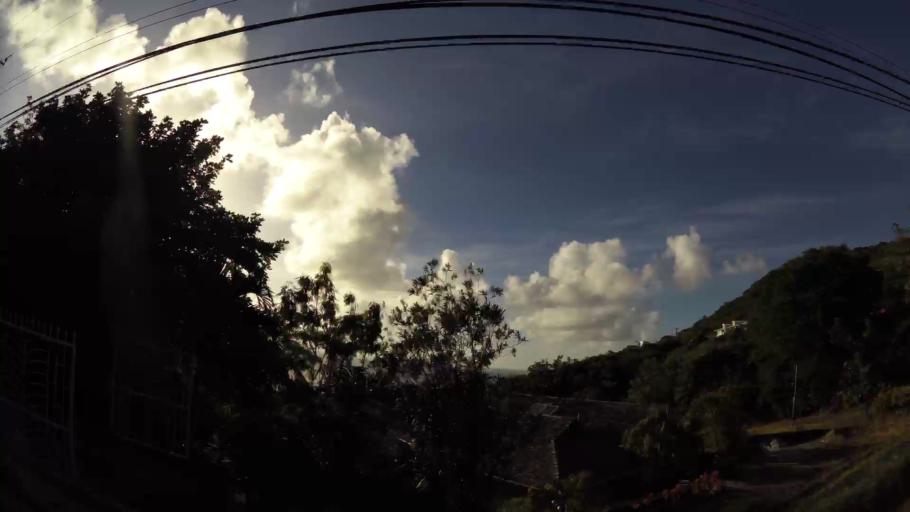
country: LC
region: Gros-Islet
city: Gros Islet
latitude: 14.1034
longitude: -60.9421
